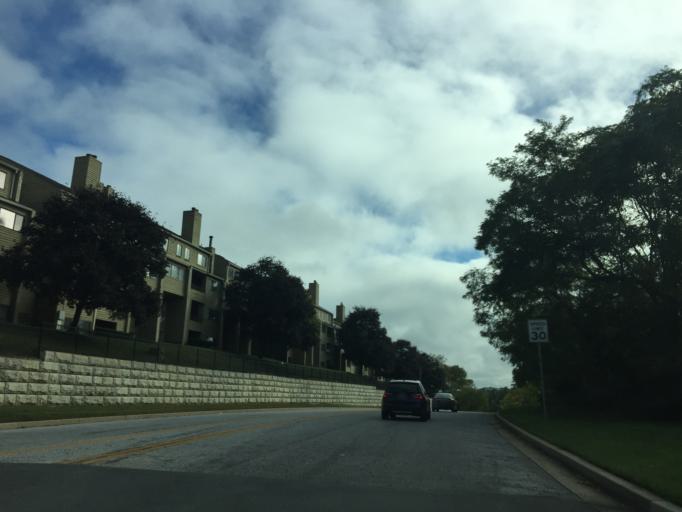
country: US
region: Maryland
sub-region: Baltimore County
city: Mays Chapel
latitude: 39.3843
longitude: -76.6671
